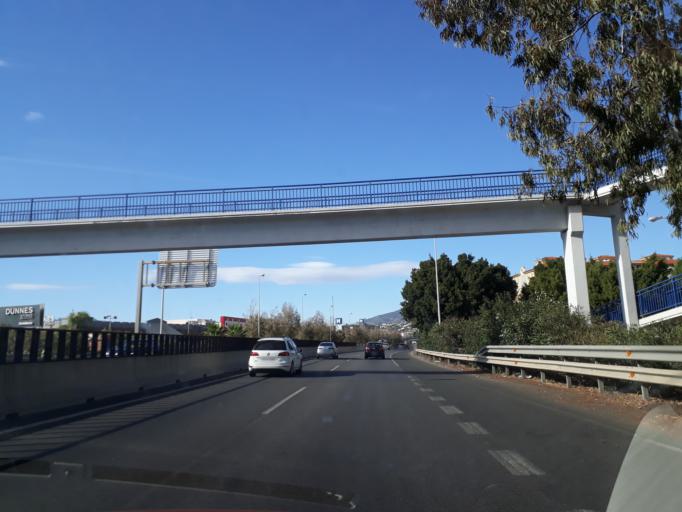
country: ES
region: Andalusia
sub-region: Provincia de Malaga
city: Fuengirola
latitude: 36.5326
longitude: -4.6319
